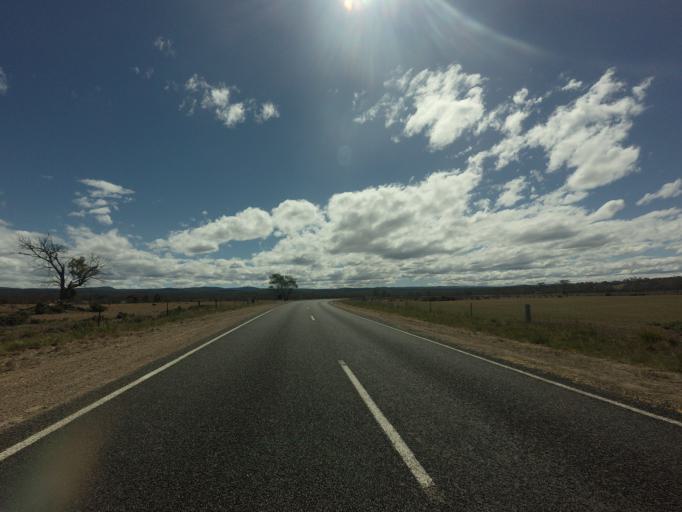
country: AU
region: Tasmania
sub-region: Break O'Day
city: St Helens
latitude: -42.0456
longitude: 148.0400
